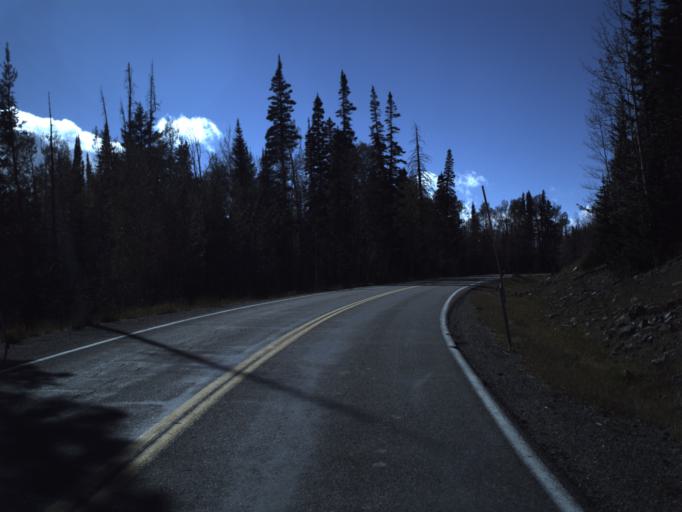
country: US
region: Utah
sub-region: Iron County
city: Parowan
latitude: 37.6555
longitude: -112.8153
